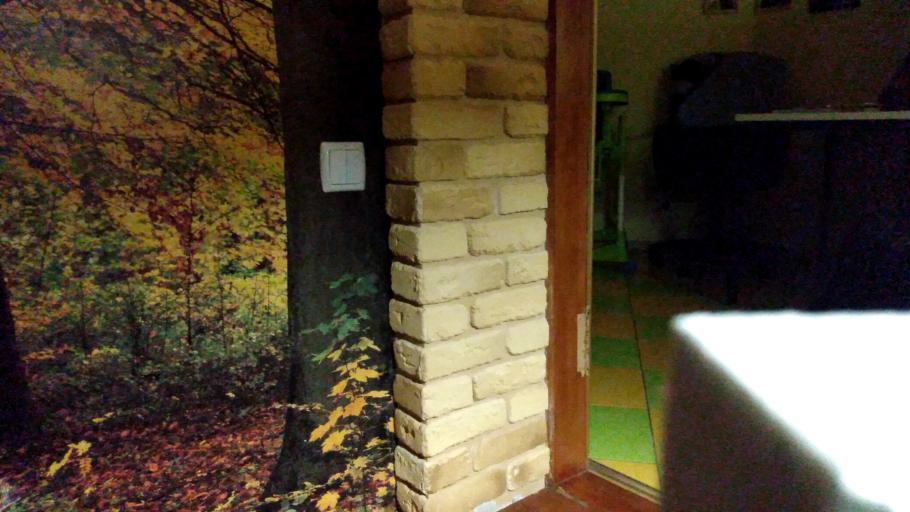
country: RU
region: Vologda
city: Lipin Bor
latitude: 60.7833
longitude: 38.0392
